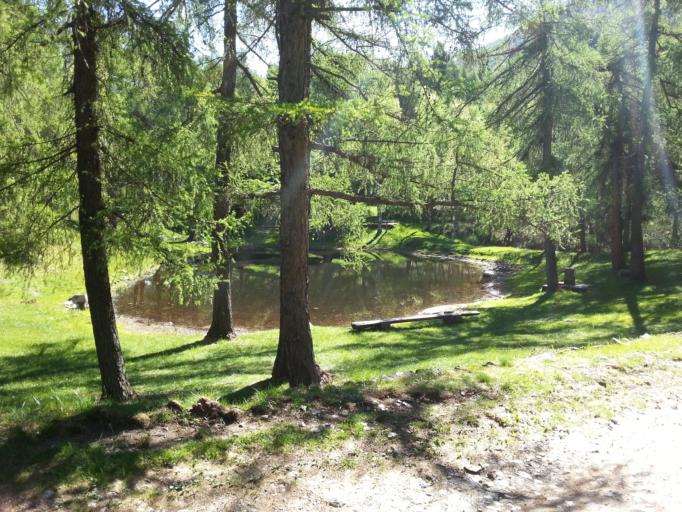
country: IT
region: Lombardy
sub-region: Provincia di Lecco
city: Sueglio
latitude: 46.0969
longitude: 9.3424
